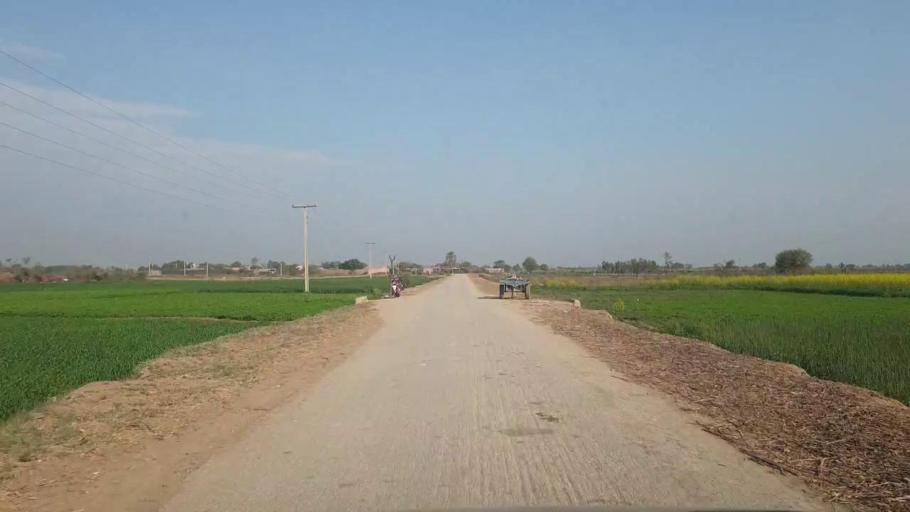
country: PK
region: Sindh
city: Tando Adam
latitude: 25.7431
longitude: 68.6071
